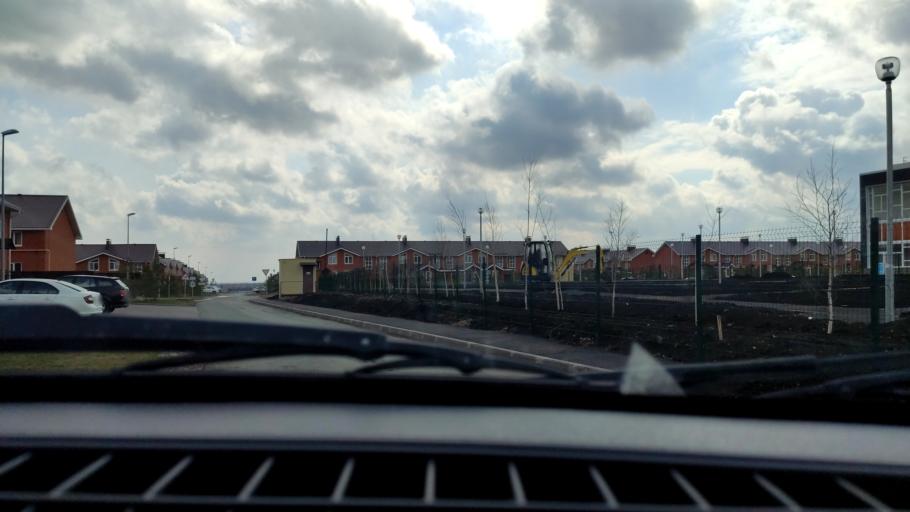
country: RU
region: Bashkortostan
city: Ufa
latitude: 54.5937
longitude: 55.9186
